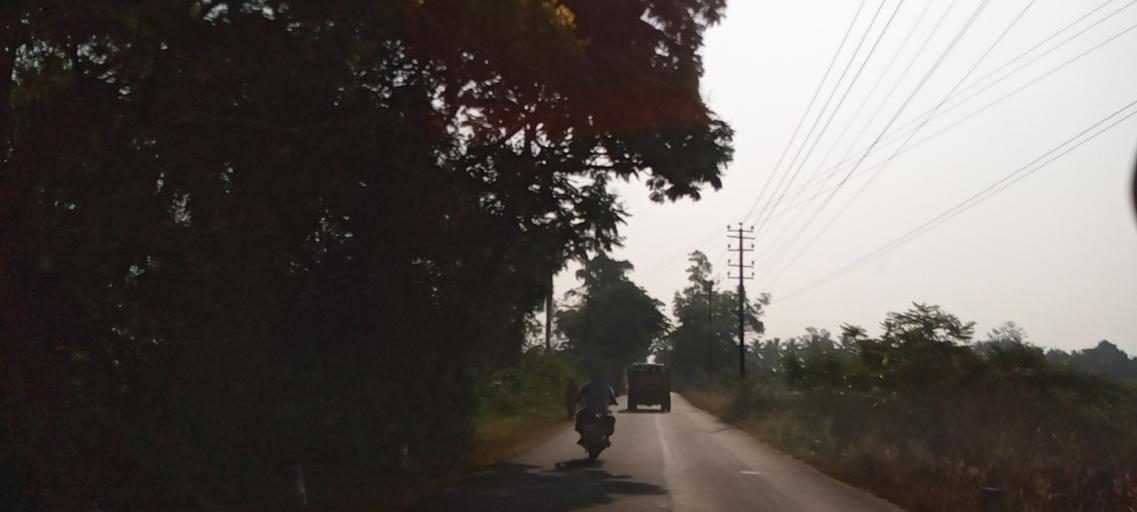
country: IN
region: Karnataka
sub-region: Udupi
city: Coondapoor
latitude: 13.5086
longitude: 74.7193
